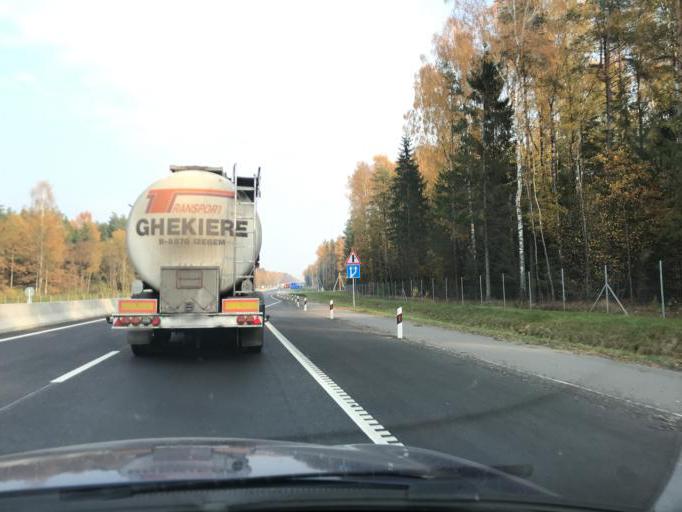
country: BY
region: Grodnenskaya
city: Shchuchin
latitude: 53.6817
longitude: 24.8481
